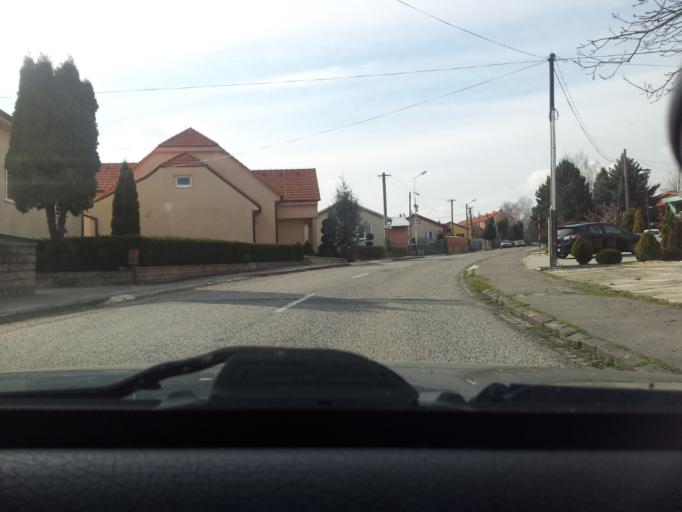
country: SK
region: Nitriansky
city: Tlmace
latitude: 48.2919
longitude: 18.5188
